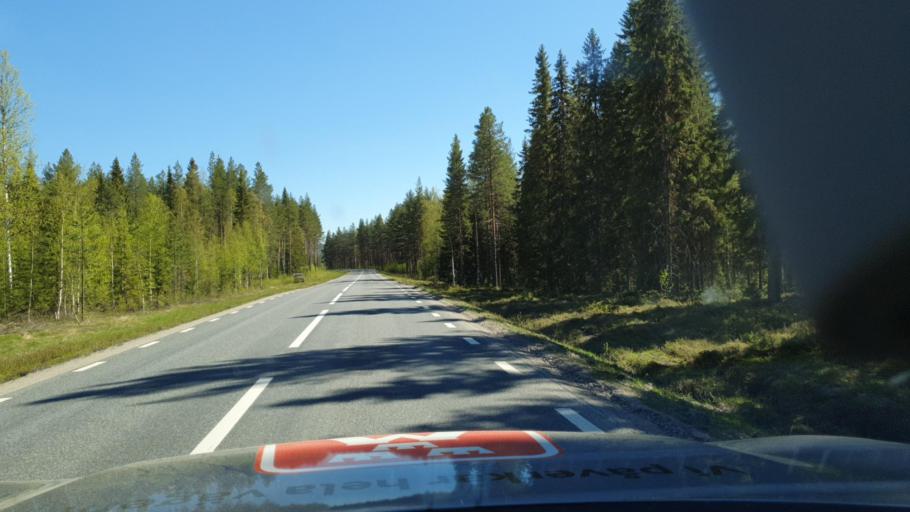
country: SE
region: Vaesternorrland
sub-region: OErnskoeldsviks Kommun
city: Bredbyn
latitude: 63.7581
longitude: 18.4804
